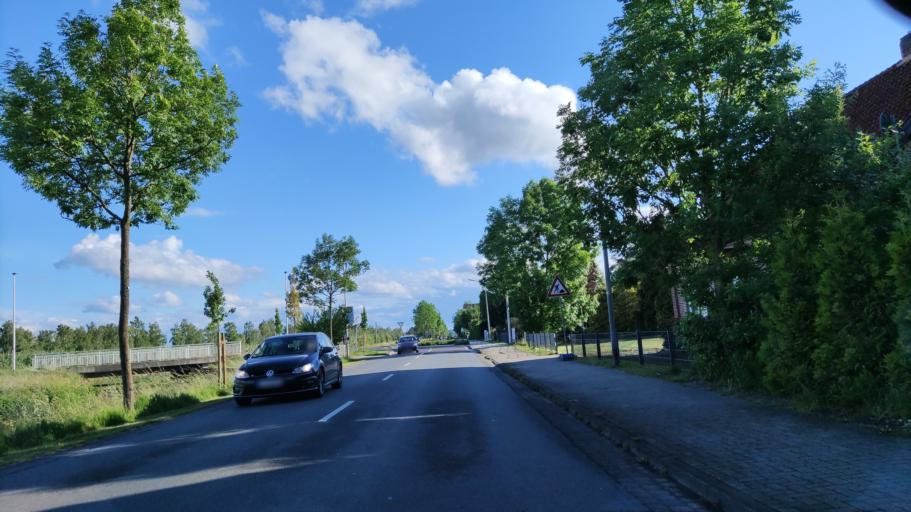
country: DE
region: Lower Saxony
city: Jork
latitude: 53.5268
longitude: 9.6768
